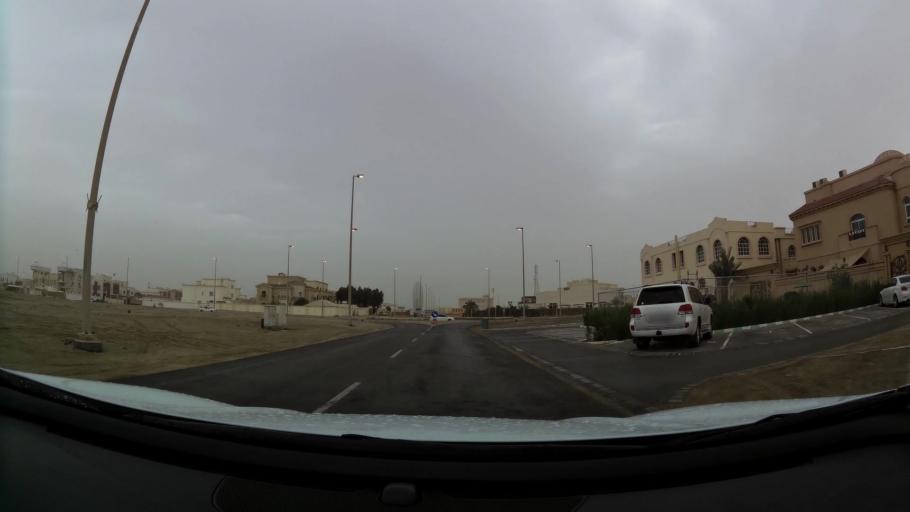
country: AE
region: Abu Dhabi
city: Abu Dhabi
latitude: 24.4281
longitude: 54.5810
